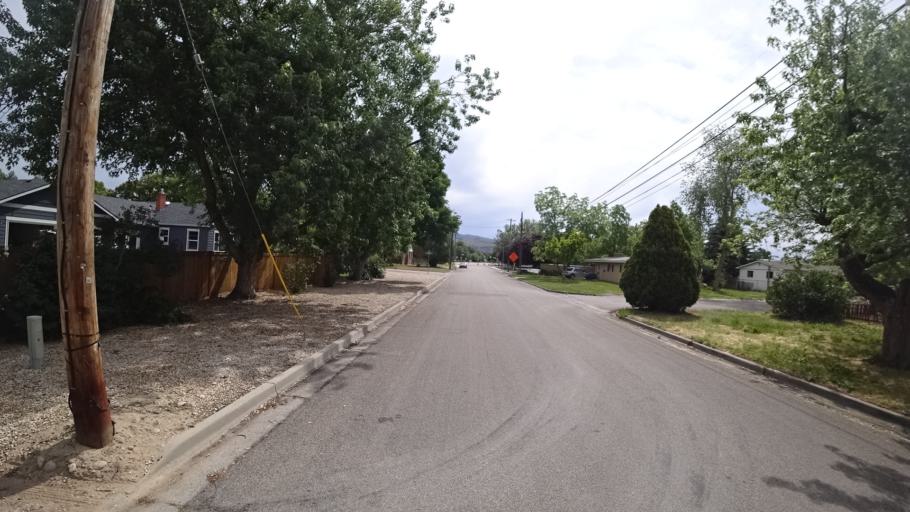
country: US
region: Idaho
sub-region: Ada County
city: Boise
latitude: 43.5899
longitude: -116.1955
